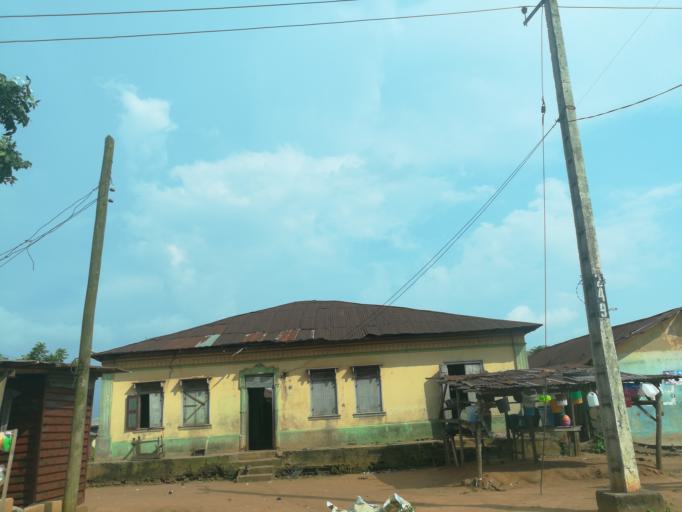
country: NG
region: Lagos
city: Ikorodu
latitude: 6.6664
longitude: 3.6725
